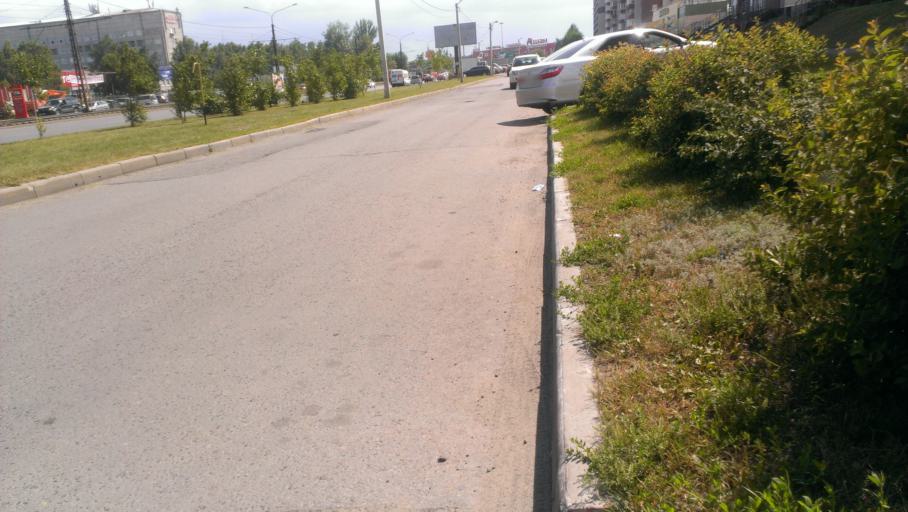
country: RU
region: Altai Krai
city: Novosilikatnyy
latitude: 53.3330
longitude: 83.6927
